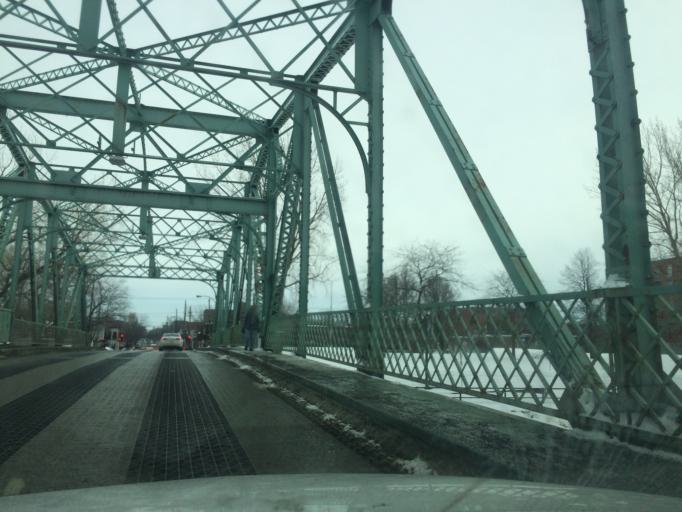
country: CA
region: Quebec
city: Westmount
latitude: 45.4806
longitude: -73.5730
